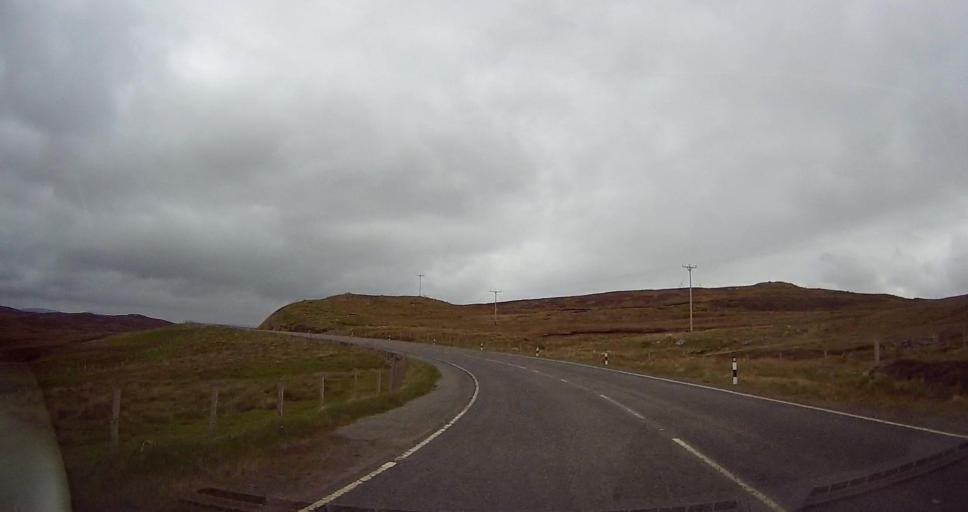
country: GB
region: Scotland
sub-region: Shetland Islands
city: Sandwick
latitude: 60.2591
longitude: -1.4891
